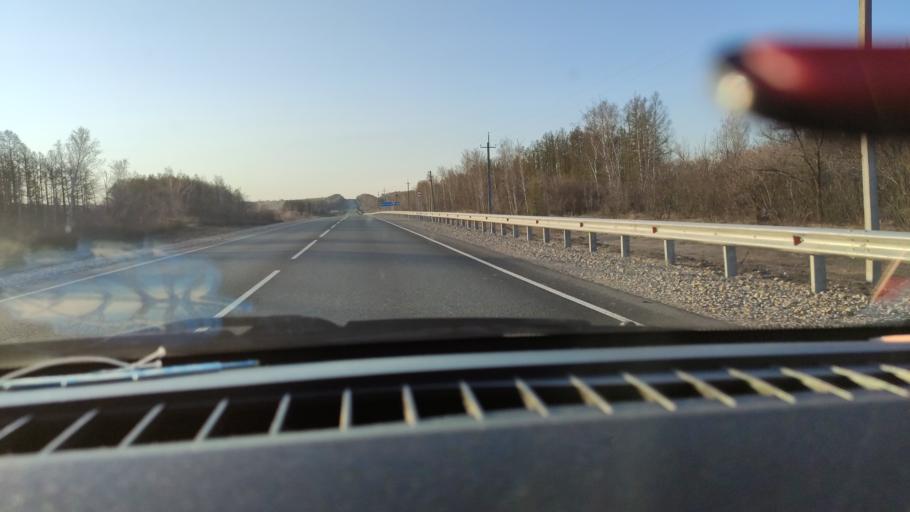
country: RU
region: Saratov
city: Shikhany
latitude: 52.1577
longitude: 47.1747
